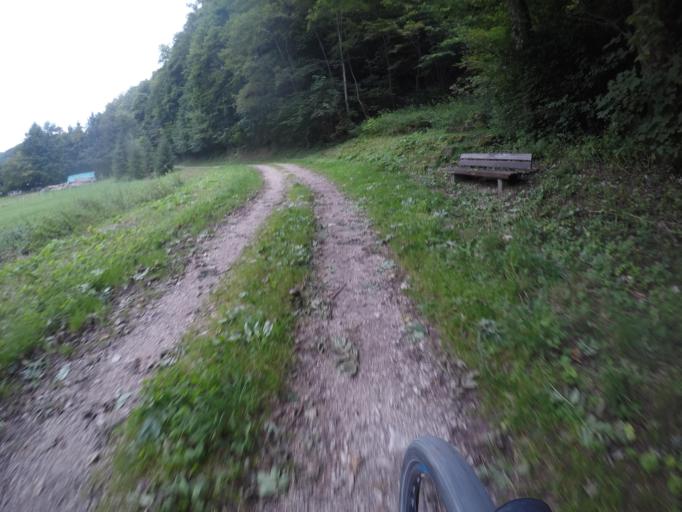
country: DE
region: Baden-Wuerttemberg
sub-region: Tuebingen Region
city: Munsingen
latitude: 48.4471
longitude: 9.4508
